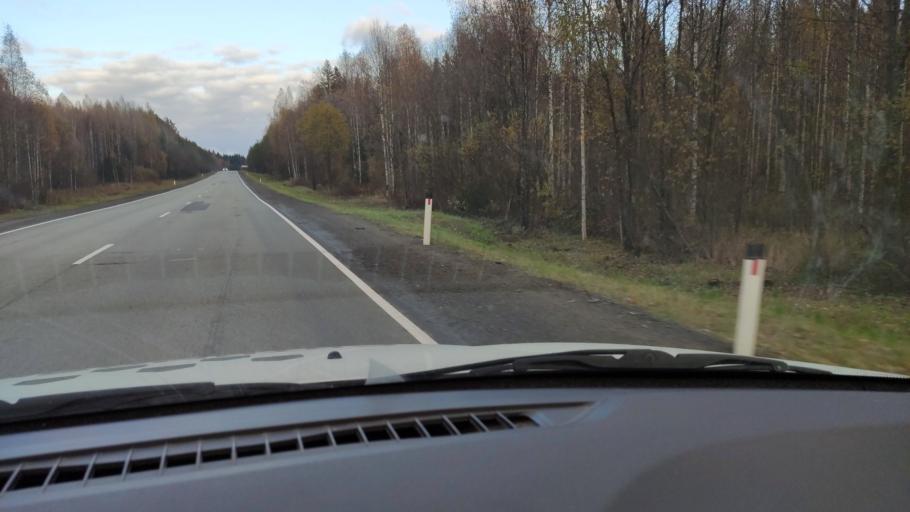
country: RU
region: Kirov
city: Belaya Kholunitsa
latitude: 58.9007
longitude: 50.9313
